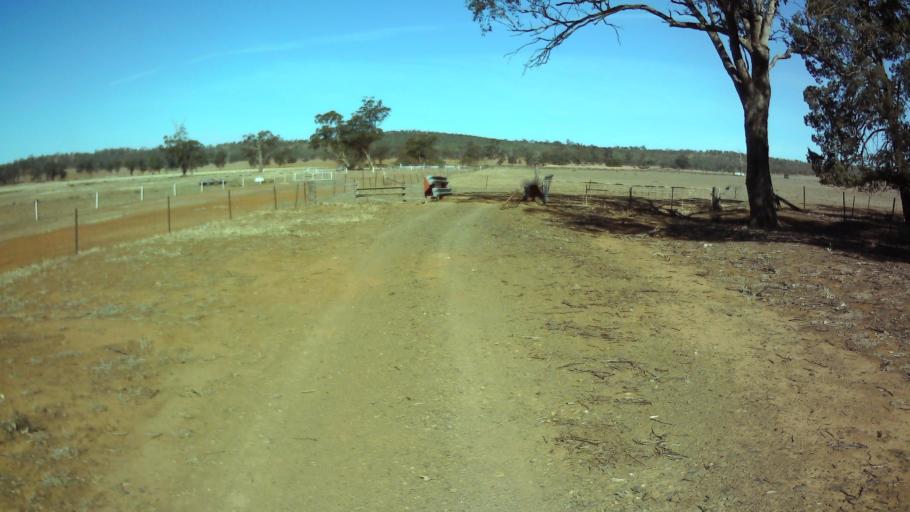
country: AU
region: New South Wales
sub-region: Weddin
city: Grenfell
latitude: -33.7807
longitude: 147.8397
